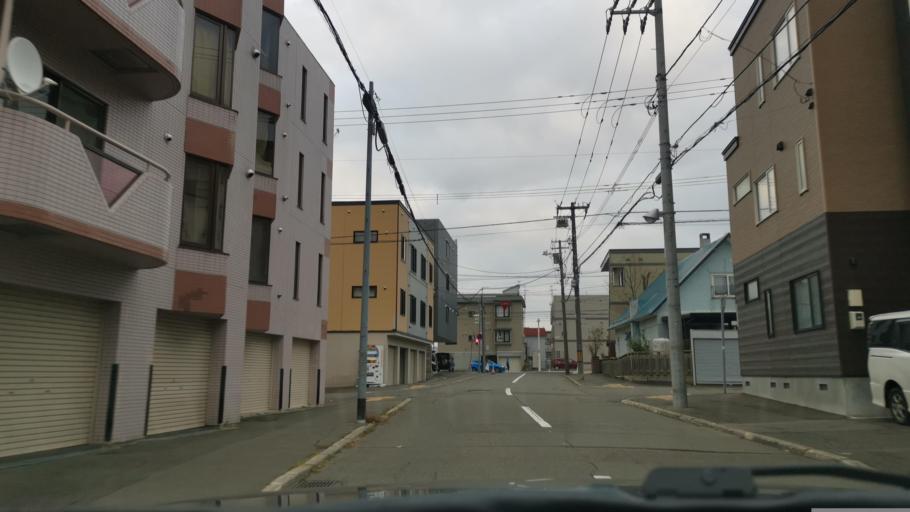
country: JP
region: Hokkaido
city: Sapporo
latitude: 43.0437
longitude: 141.4078
